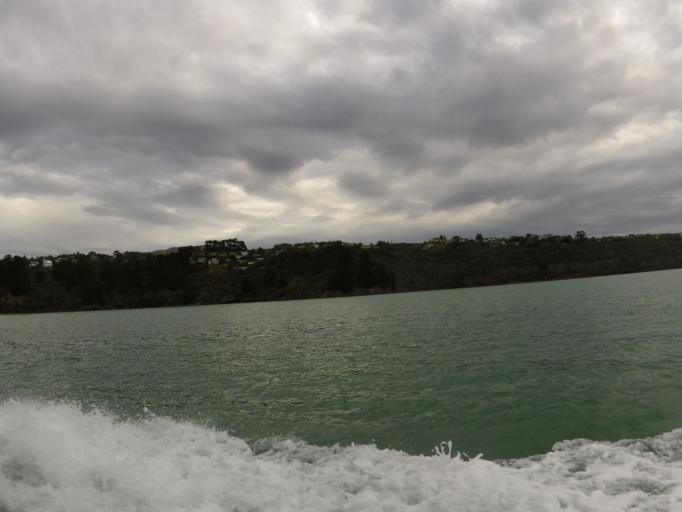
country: NZ
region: Canterbury
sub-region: Christchurch City
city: Christchurch
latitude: -43.6213
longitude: 172.7327
